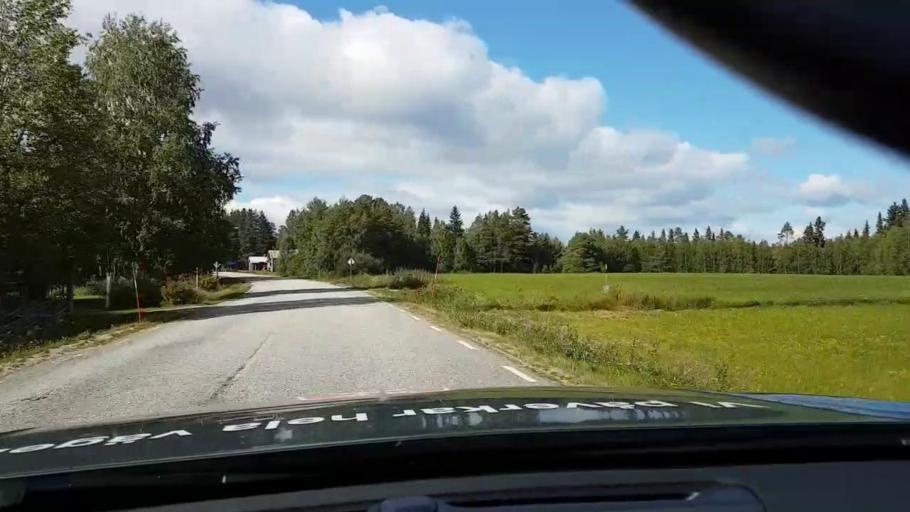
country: SE
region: Vaesterbotten
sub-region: Asele Kommun
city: Asele
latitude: 63.9356
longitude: 17.2882
